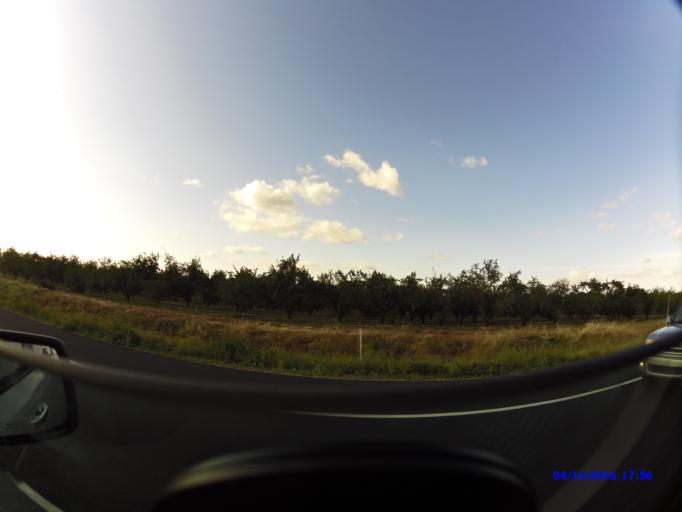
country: US
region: California
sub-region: Stanislaus County
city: Del Rio
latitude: 37.7114
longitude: -121.0185
